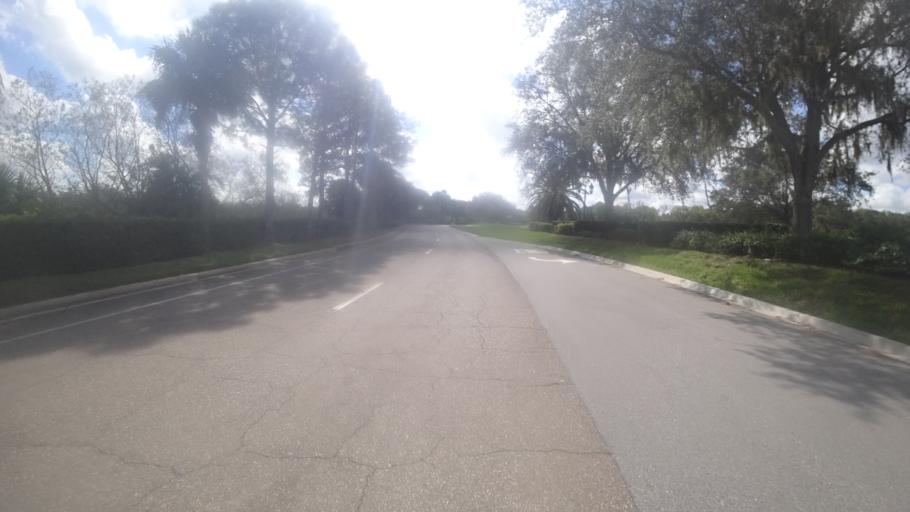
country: US
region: Florida
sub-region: Manatee County
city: Ellenton
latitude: 27.4917
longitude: -82.4644
